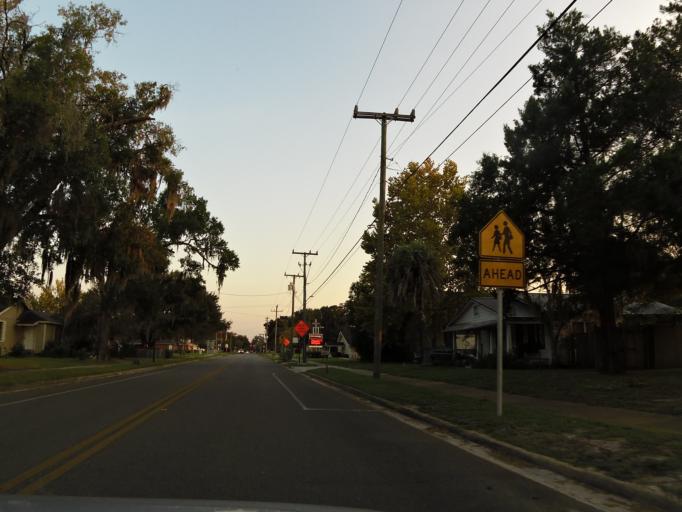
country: US
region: Florida
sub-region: Baker County
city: Macclenny
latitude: 30.2863
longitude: -82.1231
